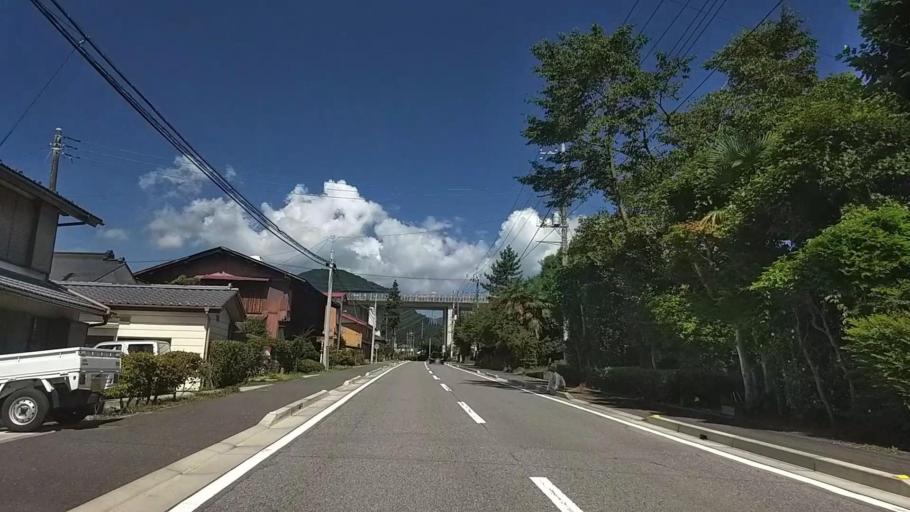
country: JP
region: Gunma
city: Annaka
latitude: 36.3428
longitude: 138.7247
